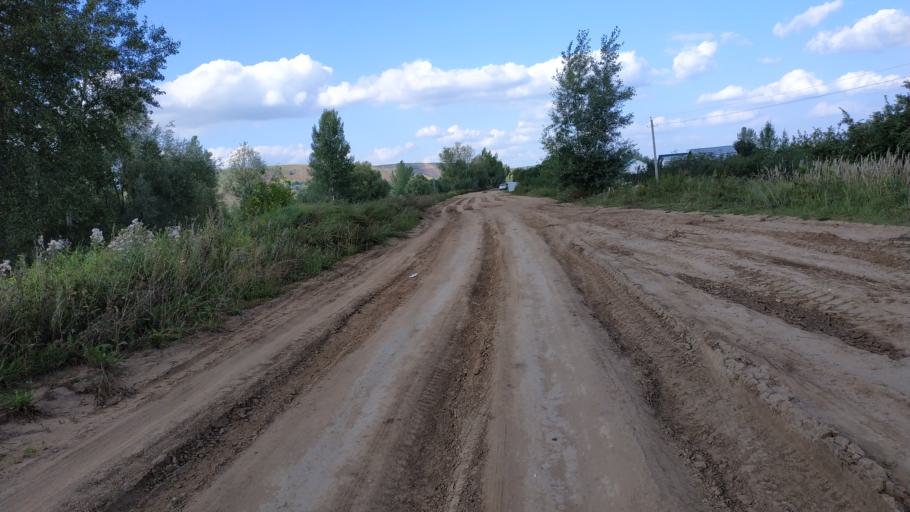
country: RU
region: Tatarstan
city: Nizhnekamsk
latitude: 55.6850
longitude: 51.7319
